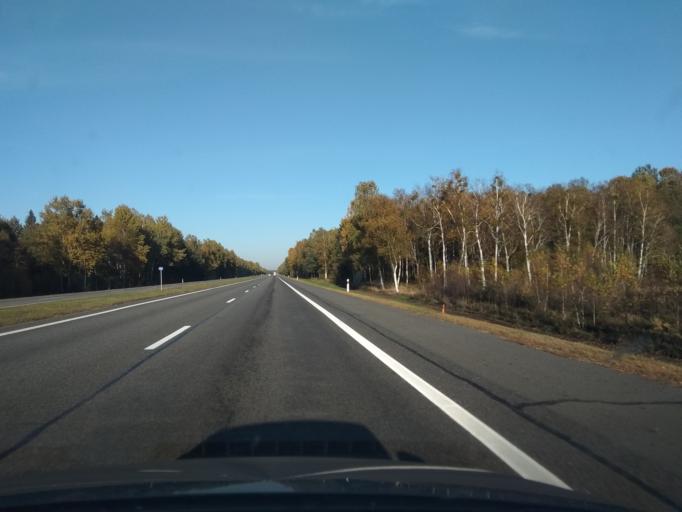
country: BY
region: Brest
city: Nyakhachava
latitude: 52.6277
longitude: 25.2067
